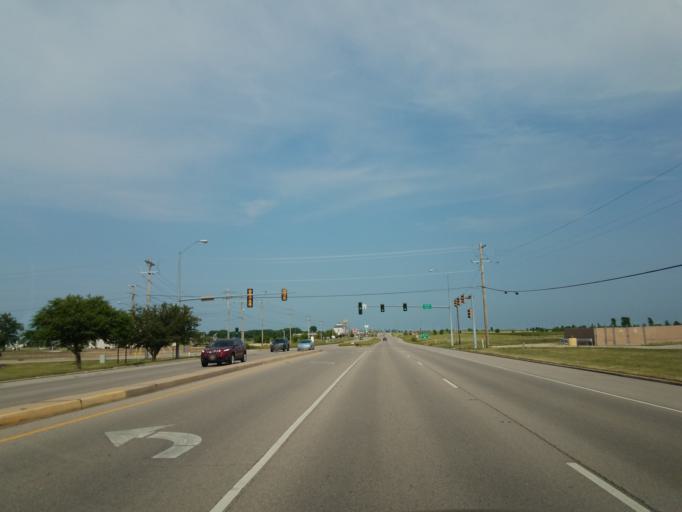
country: US
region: Illinois
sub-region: McLean County
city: Bloomington
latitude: 40.4883
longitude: -88.9247
